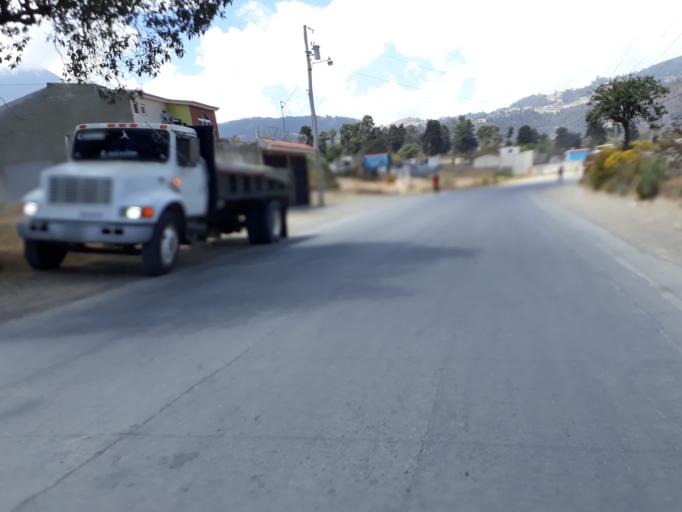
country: GT
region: Quetzaltenango
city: Quetzaltenango
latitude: 14.8191
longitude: -91.5406
